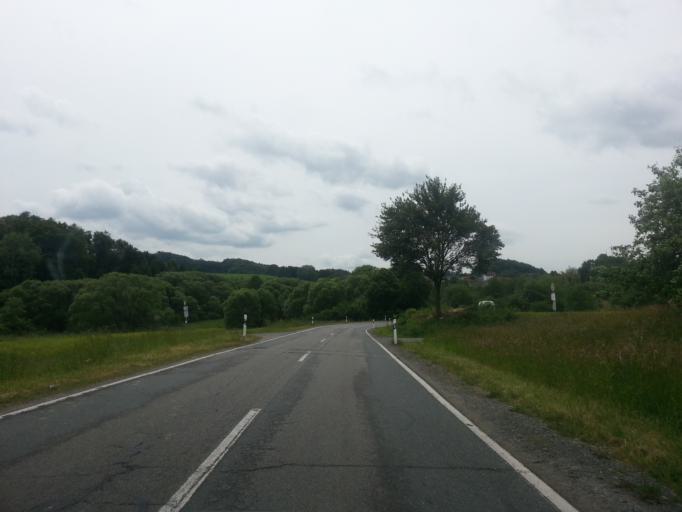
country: DE
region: Hesse
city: Lutzelbach
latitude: 49.7382
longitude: 8.7111
